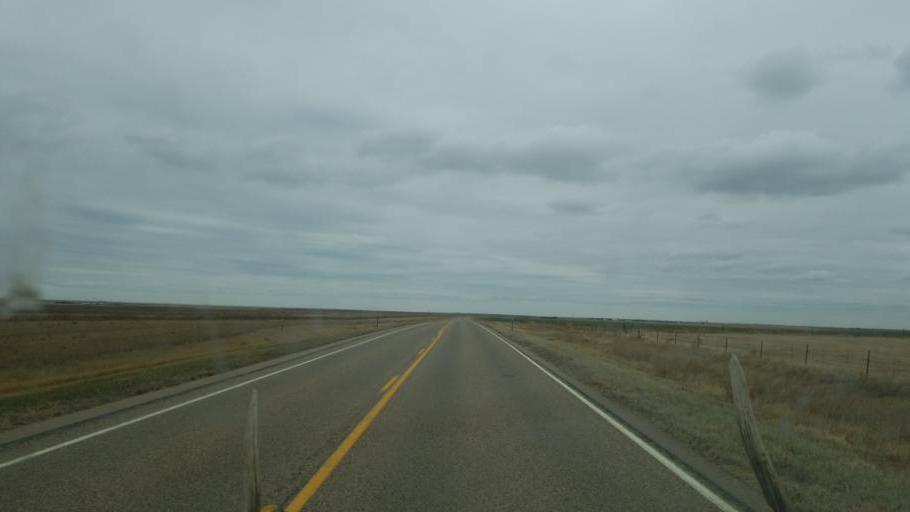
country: US
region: Colorado
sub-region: Cheyenne County
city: Cheyenne Wells
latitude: 38.8500
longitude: -102.2351
